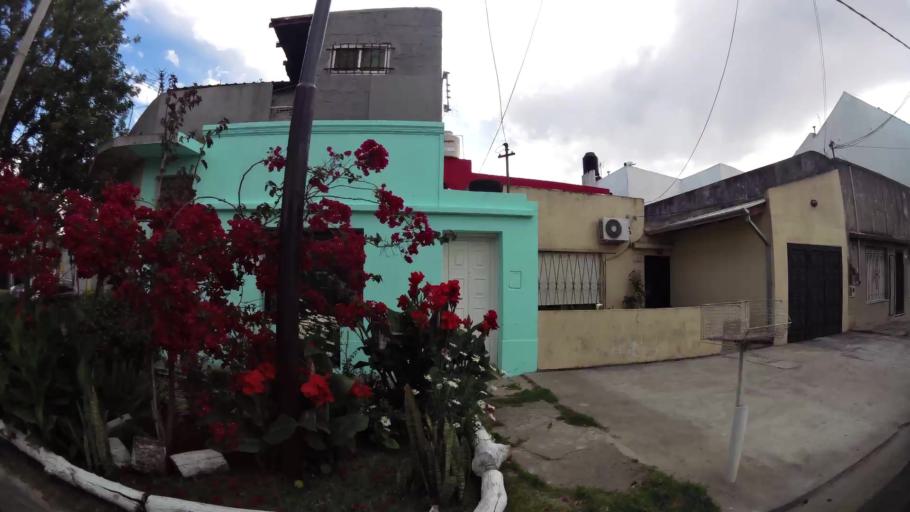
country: AR
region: Buenos Aires
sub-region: Partido de Lanus
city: Lanus
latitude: -34.6950
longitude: -58.3712
